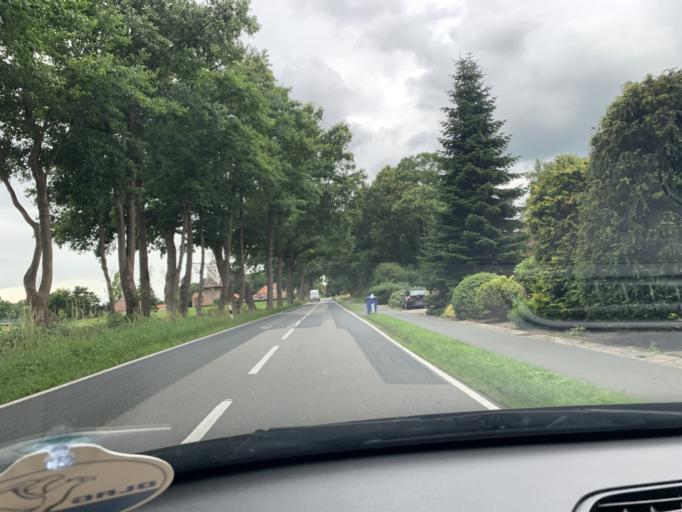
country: DE
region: Lower Saxony
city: Edewecht
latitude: 53.1309
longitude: 7.8884
